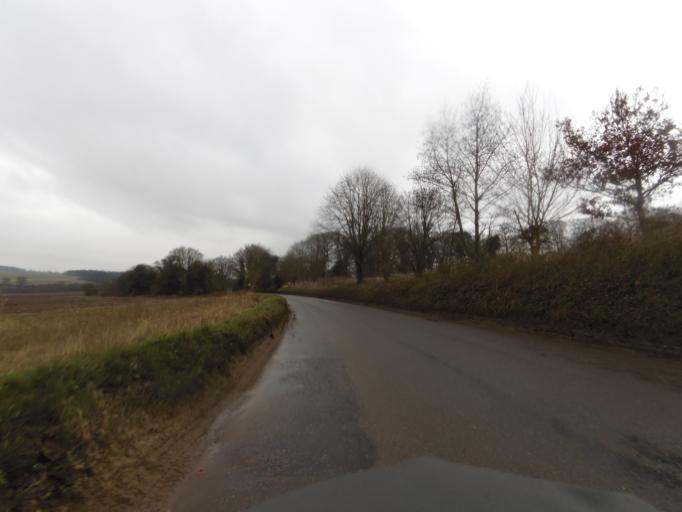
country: GB
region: England
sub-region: Norfolk
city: Briston
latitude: 52.8793
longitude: 1.0778
